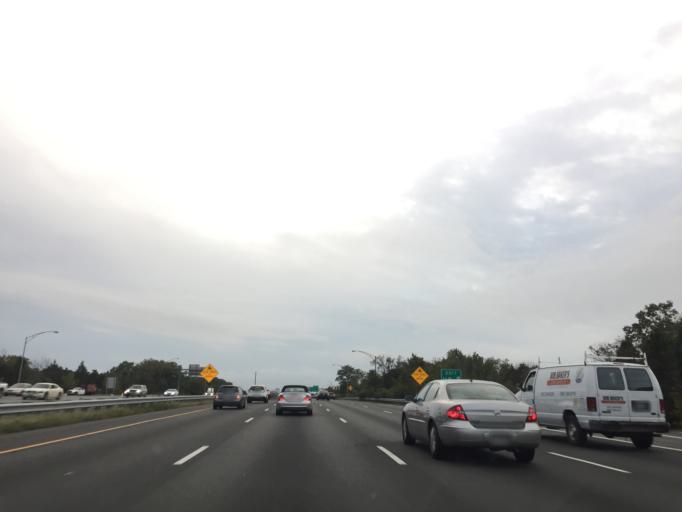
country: US
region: Maryland
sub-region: Prince George's County
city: Forestville
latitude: 38.8422
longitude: -76.8653
